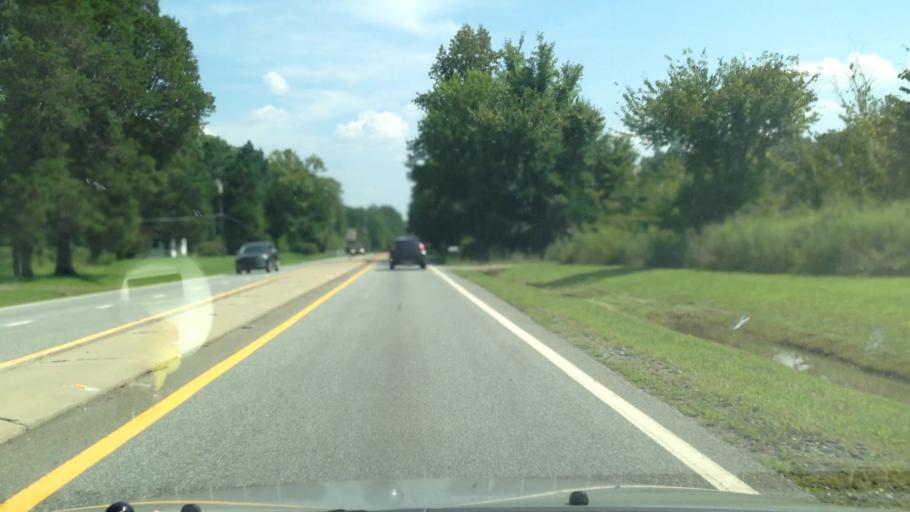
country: US
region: North Carolina
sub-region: Guilford County
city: Stokesdale
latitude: 36.2106
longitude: -79.9891
